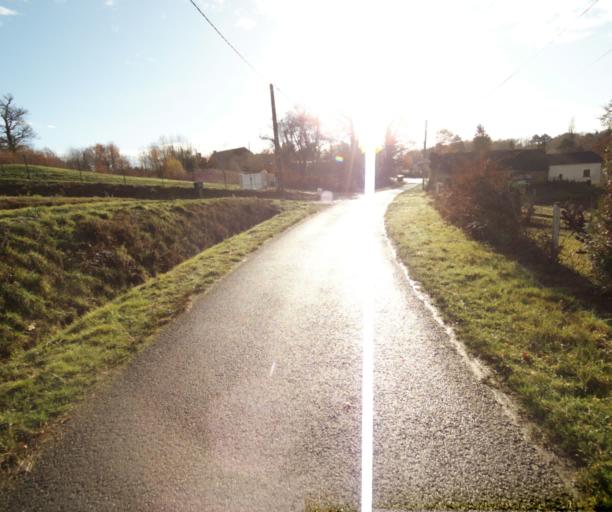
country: FR
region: Limousin
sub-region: Departement de la Correze
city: Saint-Mexant
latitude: 45.2584
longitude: 1.6292
